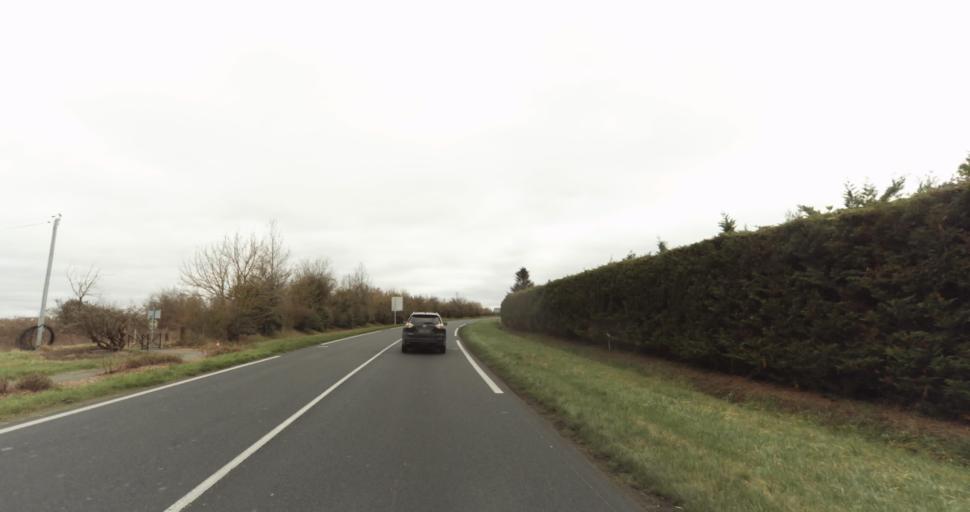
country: FR
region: Pays de la Loire
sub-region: Departement de Maine-et-Loire
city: Jumelles
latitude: 47.3812
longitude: -0.1049
